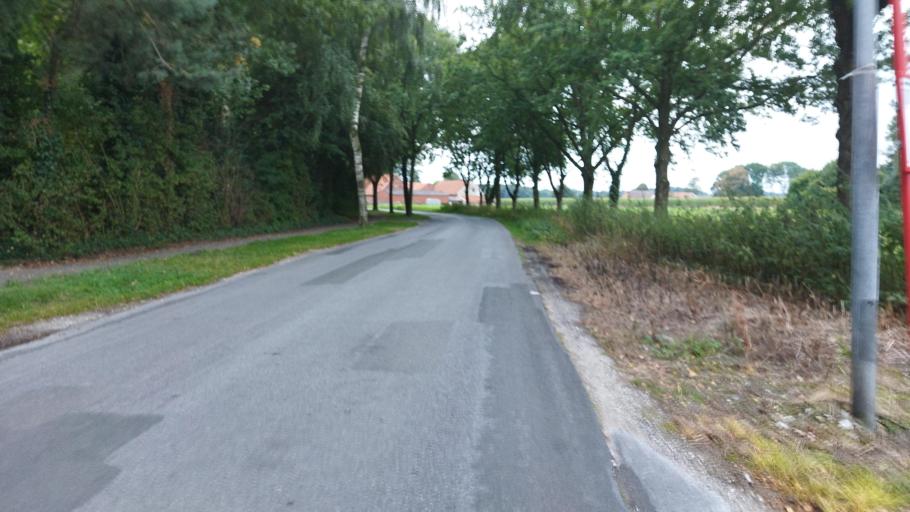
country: DE
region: Lower Saxony
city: Bad Laer
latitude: 52.0934
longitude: 8.0924
